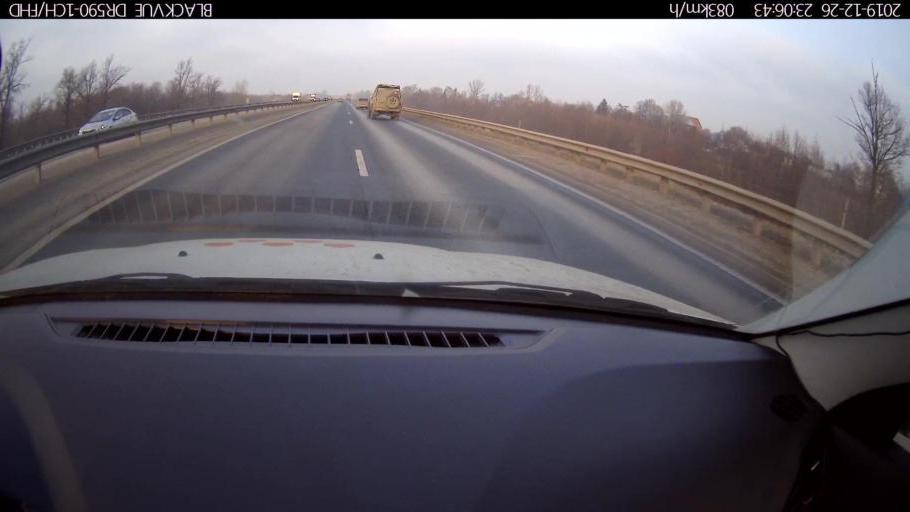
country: RU
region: Nizjnij Novgorod
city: Gorbatovka
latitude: 56.2083
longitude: 43.7518
